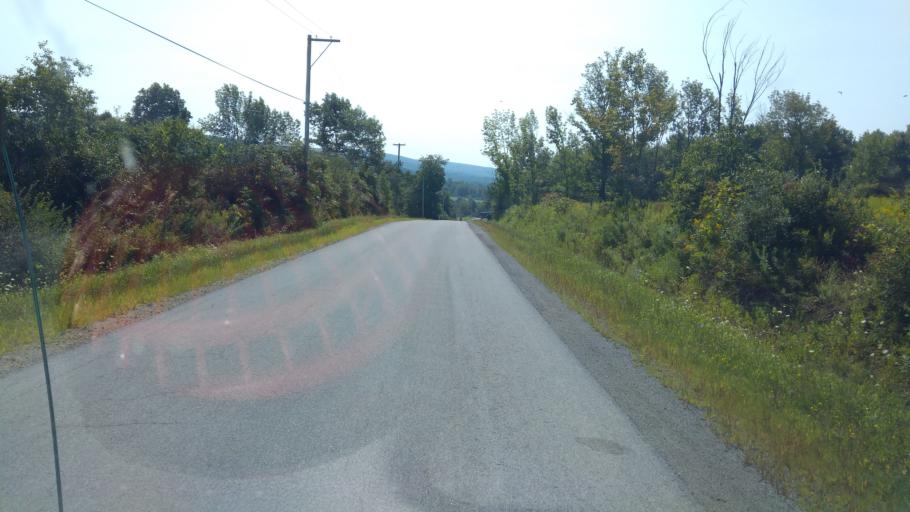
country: US
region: New York
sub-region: Allegany County
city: Belmont
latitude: 42.3336
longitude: -78.0389
